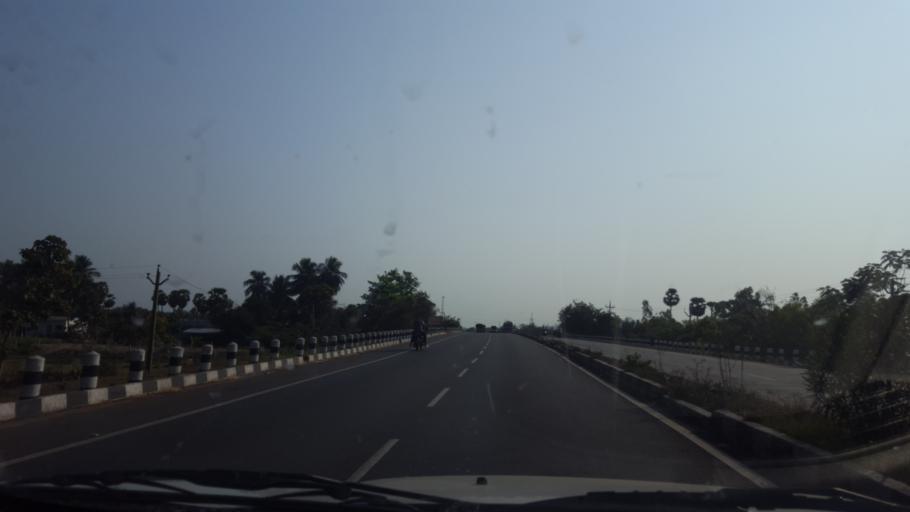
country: IN
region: Andhra Pradesh
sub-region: Vishakhapatnam
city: Elamanchili
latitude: 17.5739
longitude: 82.8633
